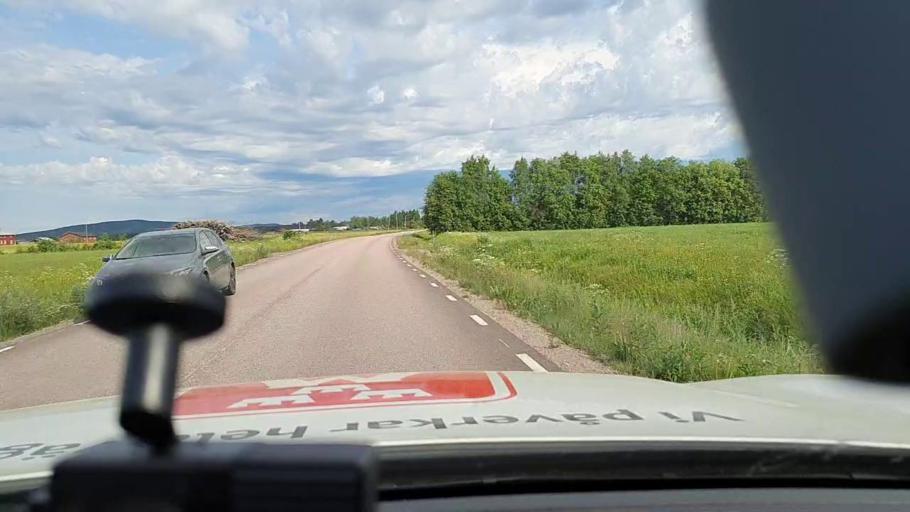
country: SE
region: Norrbotten
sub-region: Bodens Kommun
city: Saevast
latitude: 65.6989
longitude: 21.7738
